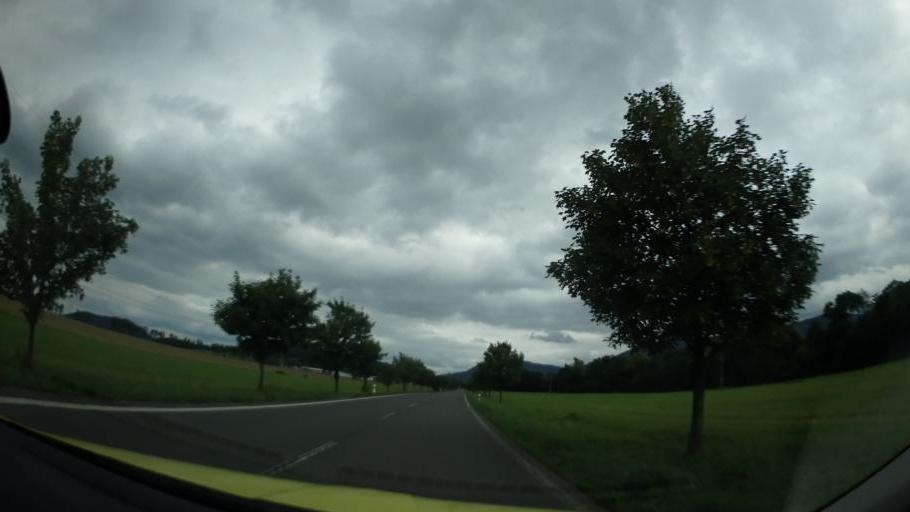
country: CZ
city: Morkov
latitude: 49.5432
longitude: 18.0799
